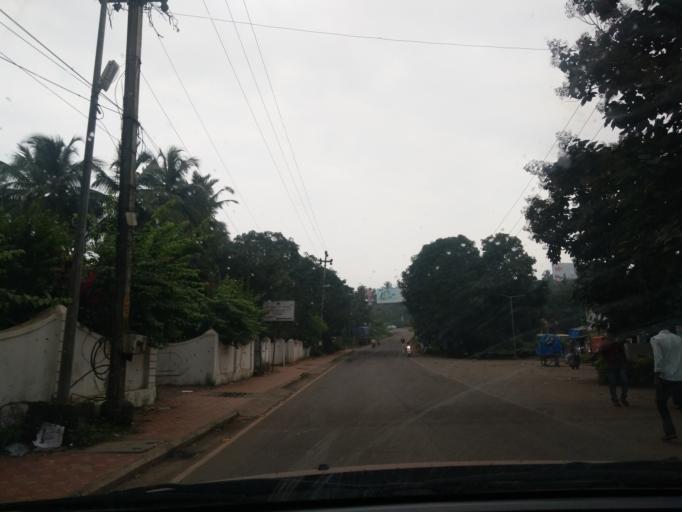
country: IN
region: Goa
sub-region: South Goa
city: Sancoale
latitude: 15.3590
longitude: 73.9271
